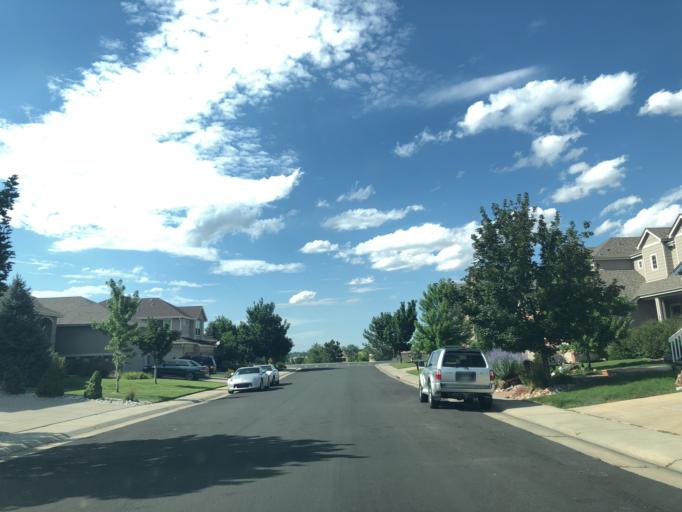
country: US
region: Colorado
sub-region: Arapahoe County
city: Dove Valley
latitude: 39.5996
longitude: -104.7833
